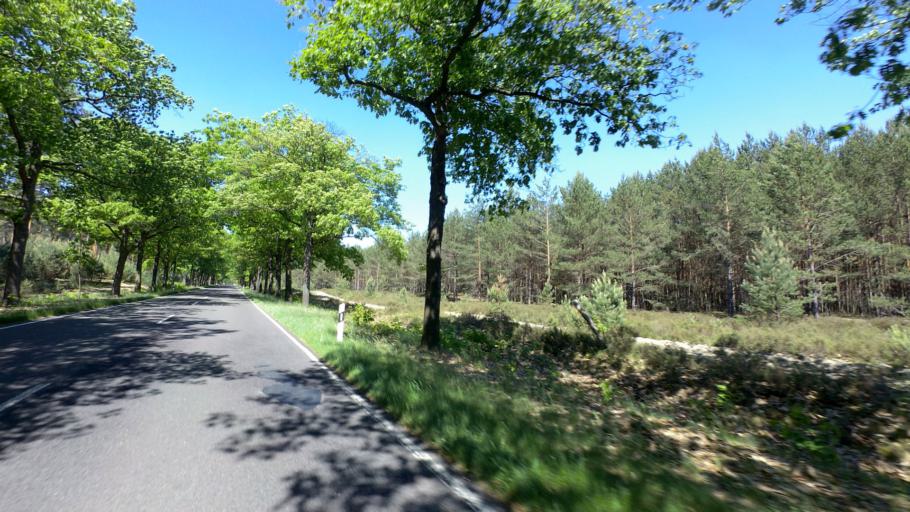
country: DE
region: Brandenburg
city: Drachhausen
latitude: 51.9049
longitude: 14.3548
